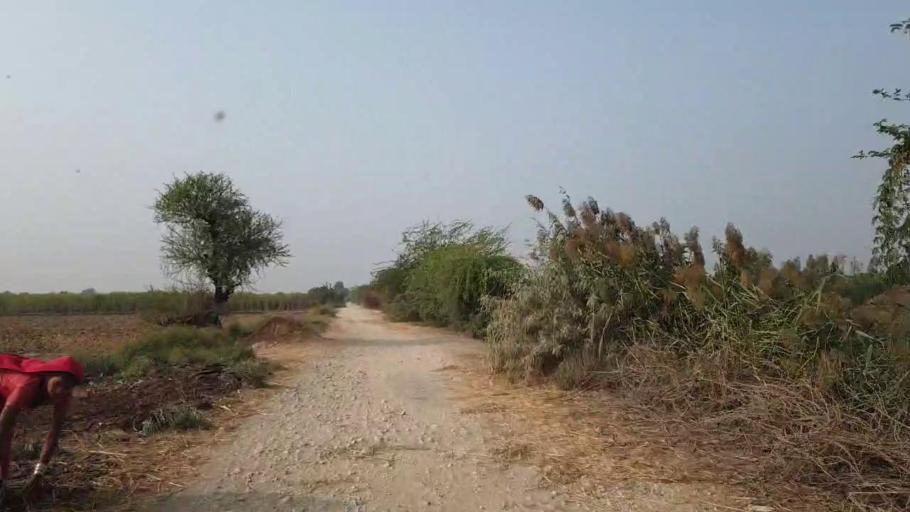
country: PK
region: Sindh
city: Tando Muhammad Khan
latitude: 25.0786
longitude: 68.5897
